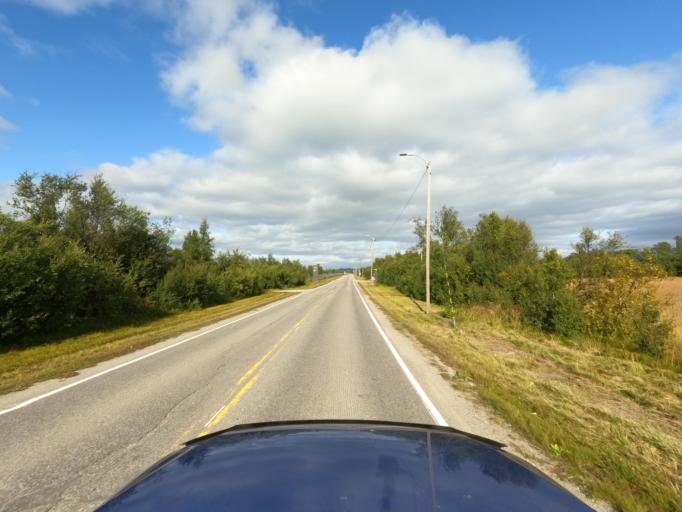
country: NO
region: Finnmark Fylke
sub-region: Porsanger
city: Lakselv
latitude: 70.0521
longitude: 24.9802
